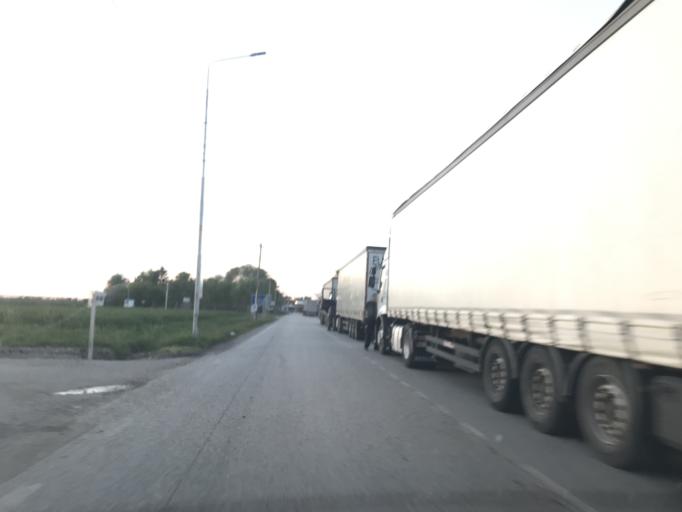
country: RS
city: Srpska Crnja
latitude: 45.7472
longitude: 20.6998
